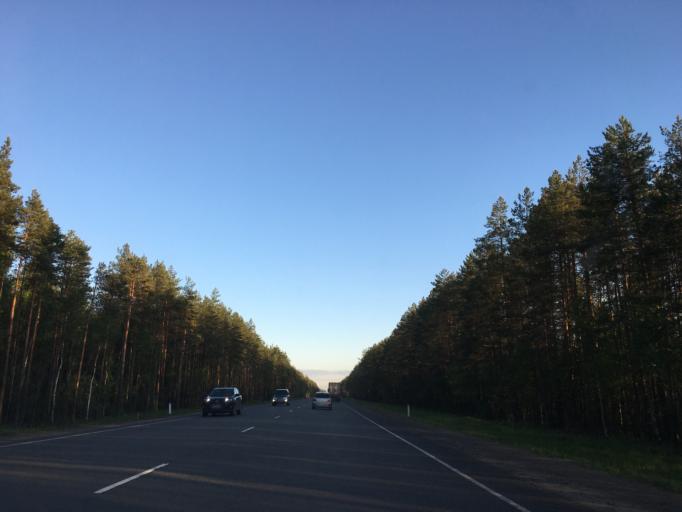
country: RU
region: Leningrad
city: Rozhdestveno
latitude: 59.2942
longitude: 29.9403
